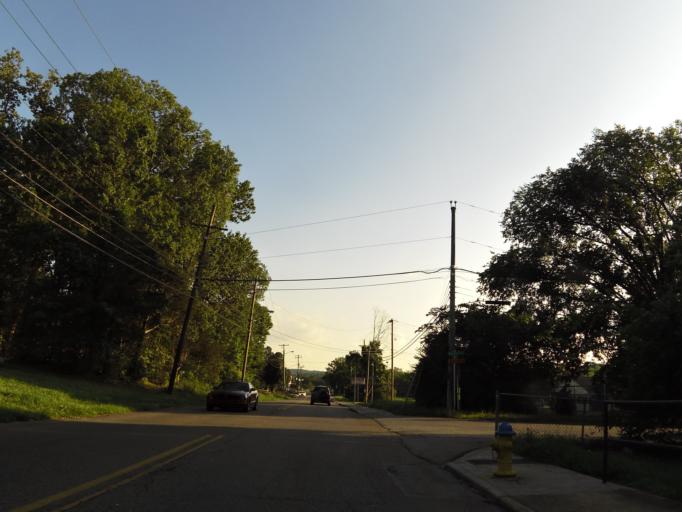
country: US
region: Tennessee
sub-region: Knox County
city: Knoxville
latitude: 35.9926
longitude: -83.9983
